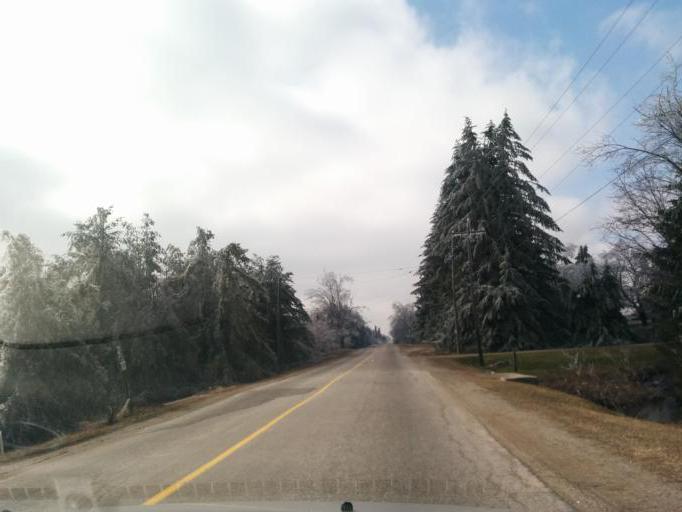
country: CA
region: Ontario
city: Waterloo
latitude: 43.6336
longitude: -80.5574
